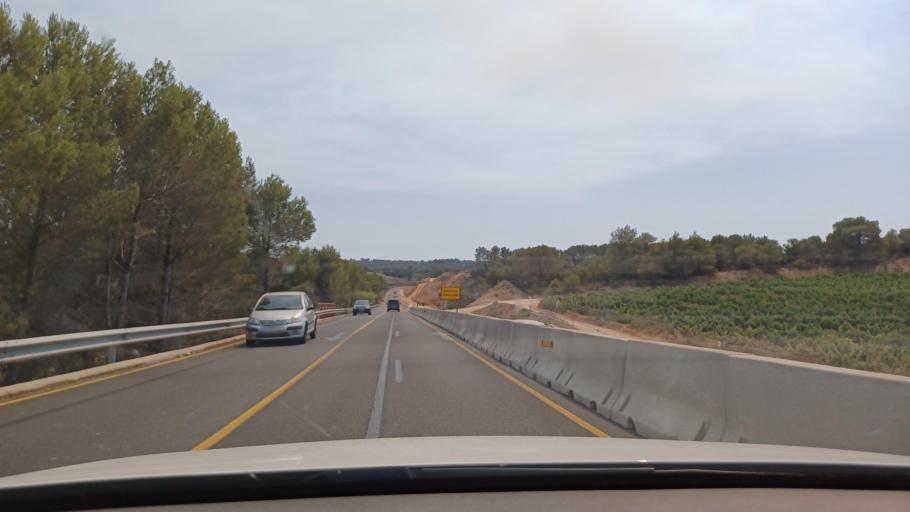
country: ES
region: Catalonia
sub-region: Provincia de Barcelona
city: Sant Pere de Riudebitlles
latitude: 41.4919
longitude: 1.7053
